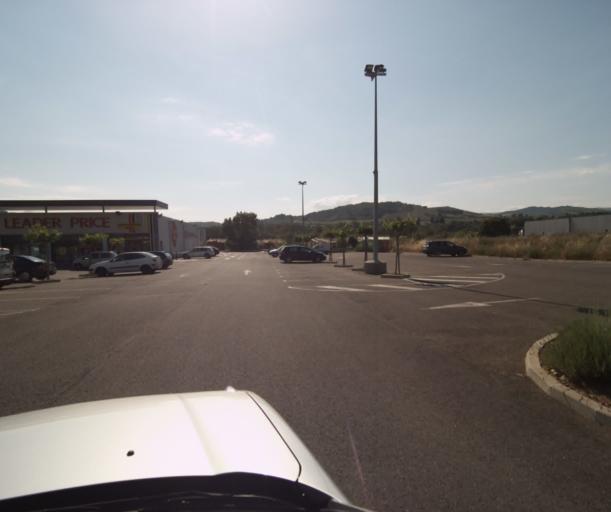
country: FR
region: Languedoc-Roussillon
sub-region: Departement de l'Aude
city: Limoux
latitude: 43.0771
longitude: 2.2235
